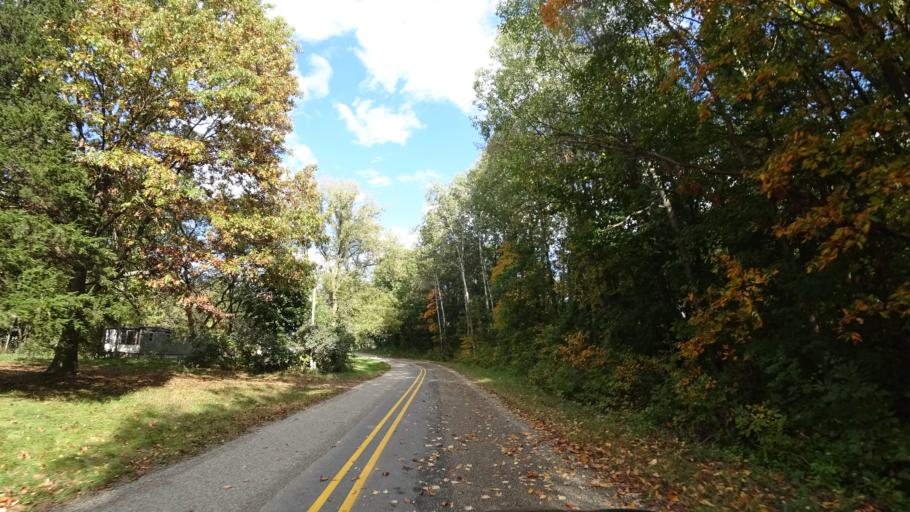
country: US
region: Michigan
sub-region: Saint Joseph County
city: Three Rivers
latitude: 41.9415
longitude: -85.6024
